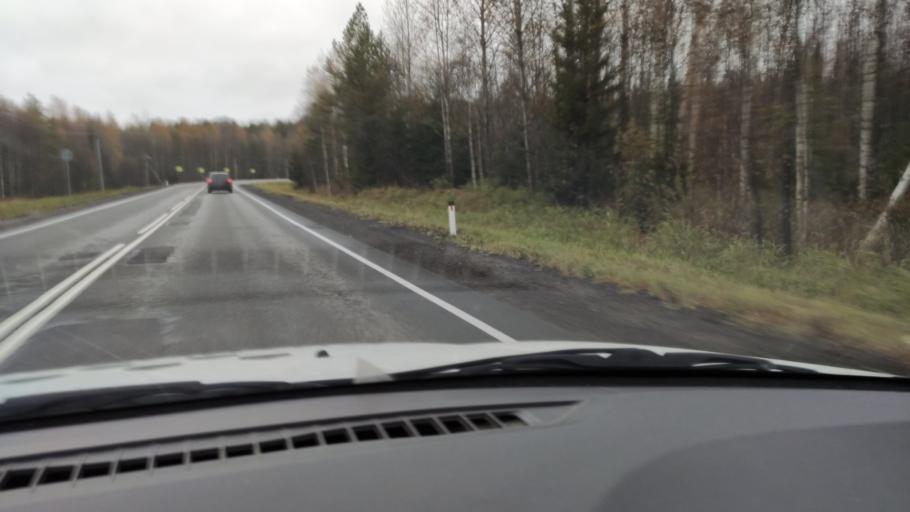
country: RU
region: Kirov
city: Belaya Kholunitsa
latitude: 58.9054
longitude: 51.0322
